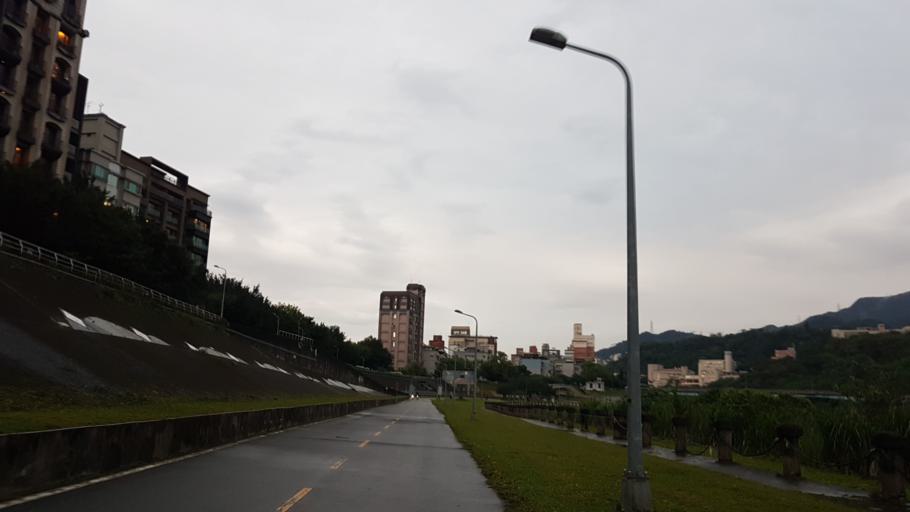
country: TW
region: Taipei
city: Taipei
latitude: 24.9813
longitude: 121.5634
